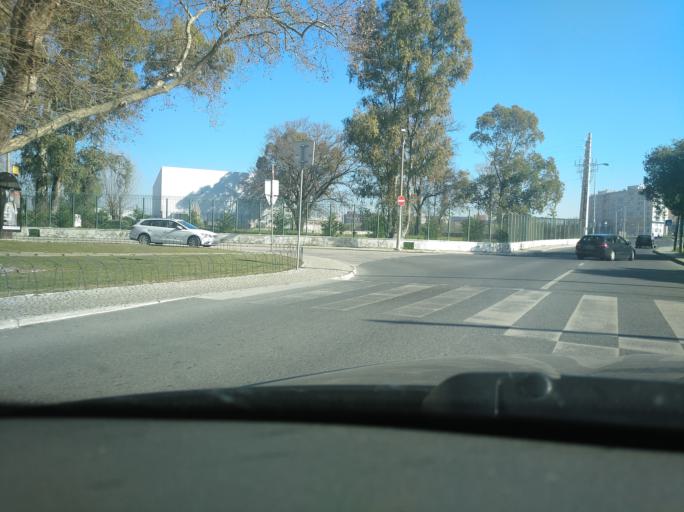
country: PT
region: Lisbon
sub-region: Odivelas
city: Pontinha
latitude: 38.7691
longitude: -9.1894
